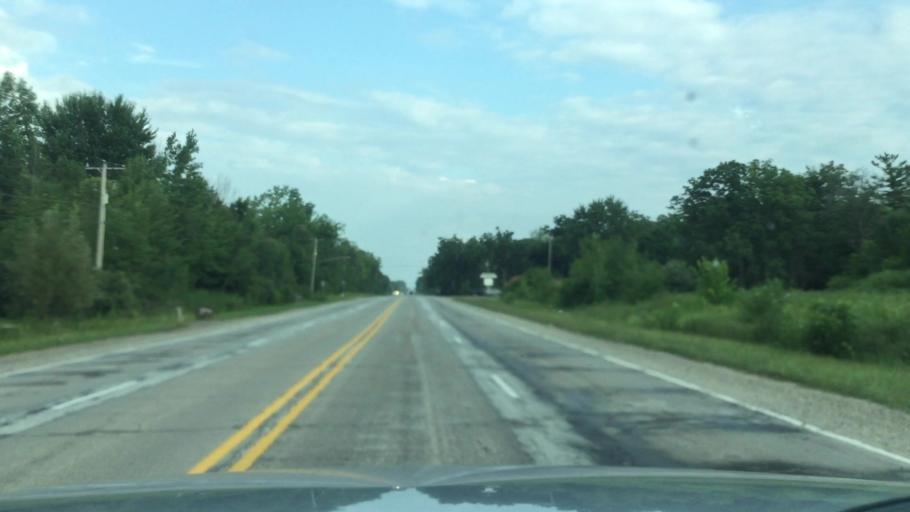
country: US
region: Michigan
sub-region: Saginaw County
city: Birch Run
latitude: 43.2804
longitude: -83.7922
